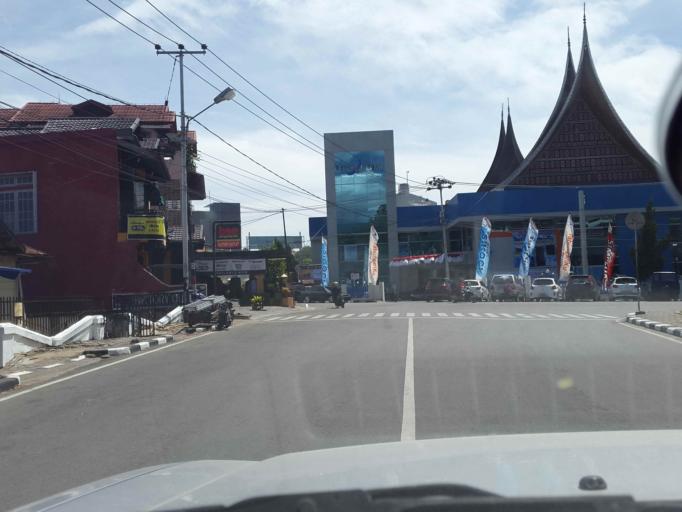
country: ID
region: West Sumatra
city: Bukittinggi
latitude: -0.3059
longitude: 100.3677
